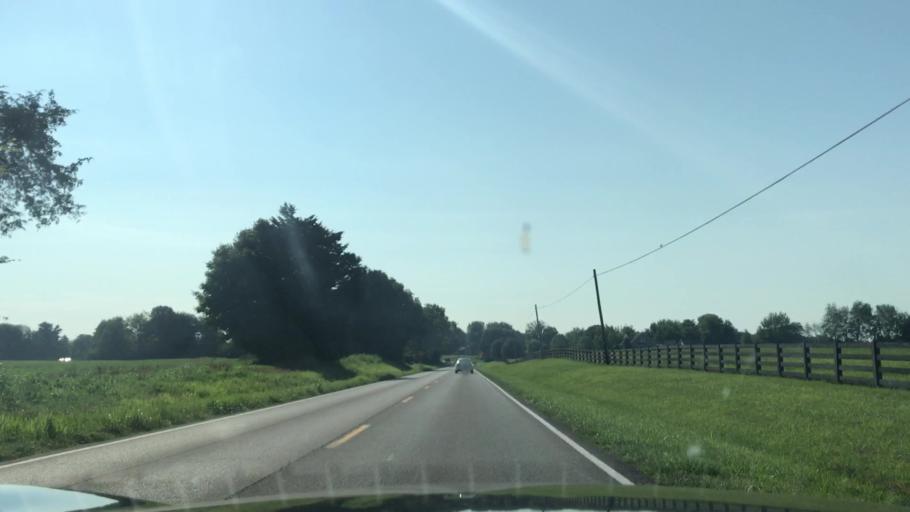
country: US
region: Kentucky
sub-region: Hart County
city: Horse Cave
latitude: 37.1683
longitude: -85.8482
